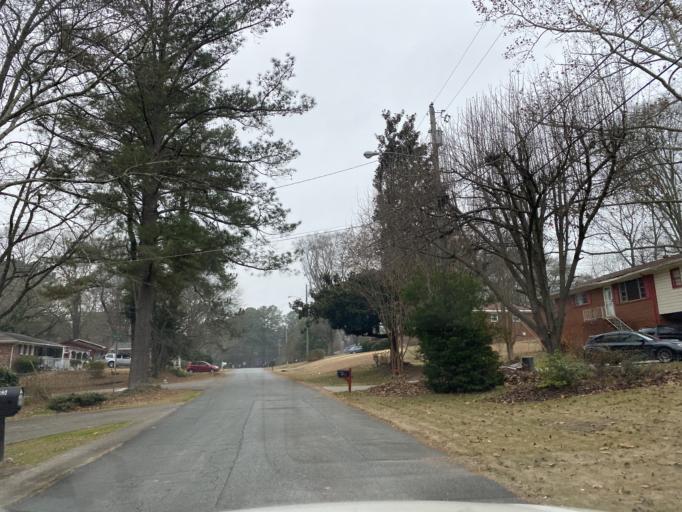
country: US
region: Georgia
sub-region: Cobb County
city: Fair Oaks
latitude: 33.9090
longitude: -84.5723
